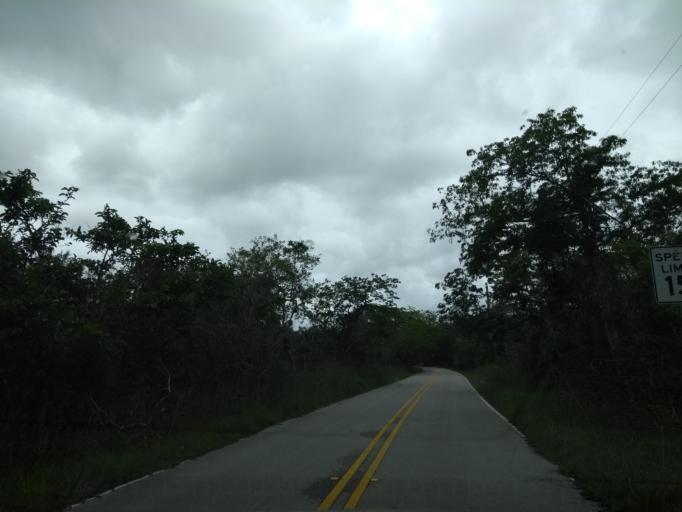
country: US
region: Florida
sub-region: Miami-Dade County
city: The Hammocks
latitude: 25.7612
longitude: -80.9202
